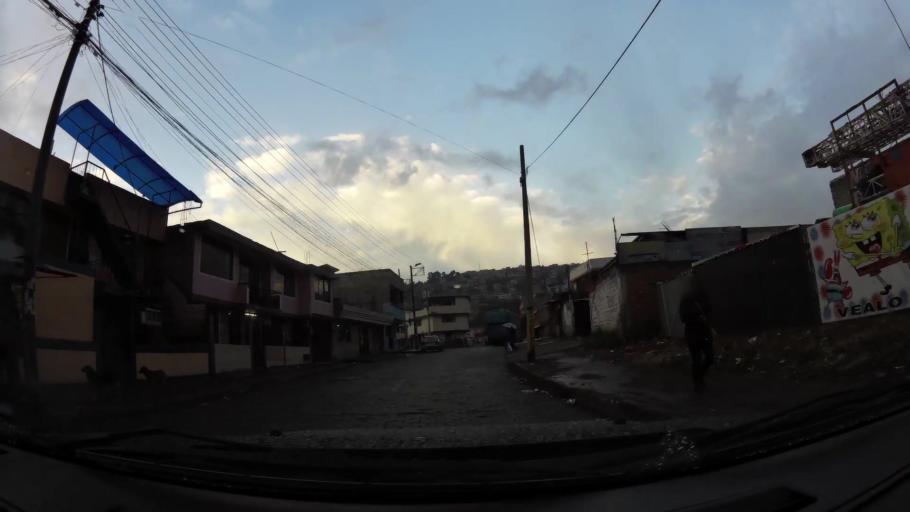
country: EC
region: Pichincha
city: Quito
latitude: -0.2971
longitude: -78.5394
